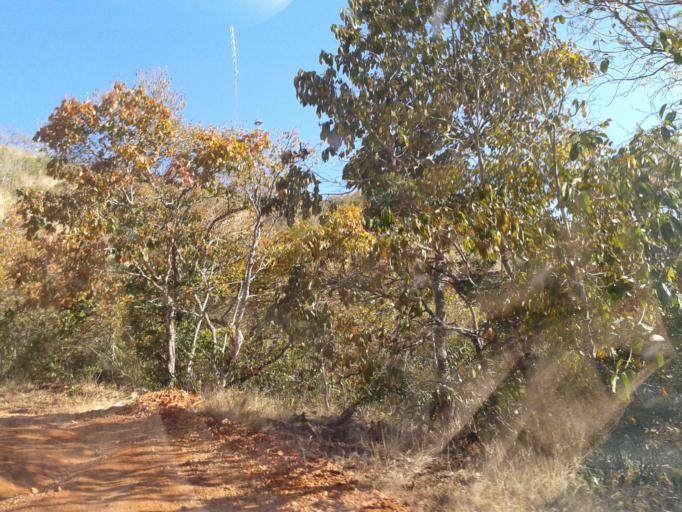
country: BR
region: Minas Gerais
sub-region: Capinopolis
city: Capinopolis
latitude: -18.7595
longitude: -49.5393
